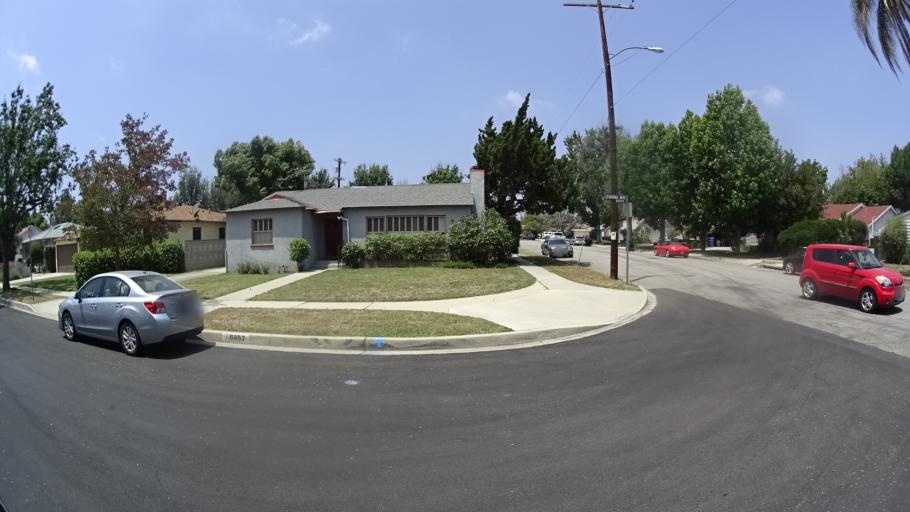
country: US
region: California
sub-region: Los Angeles County
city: Van Nuys
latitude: 34.1920
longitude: -118.4597
